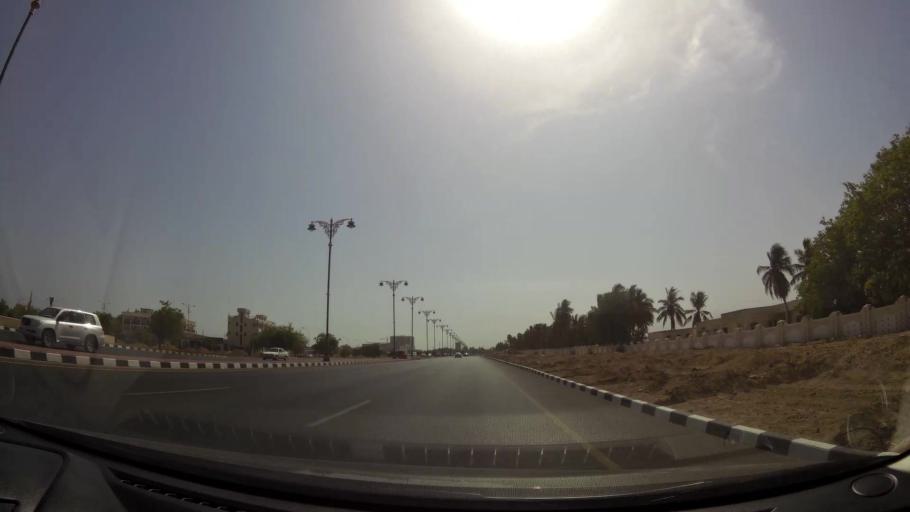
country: OM
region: Zufar
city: Salalah
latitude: 17.0248
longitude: 54.1211
